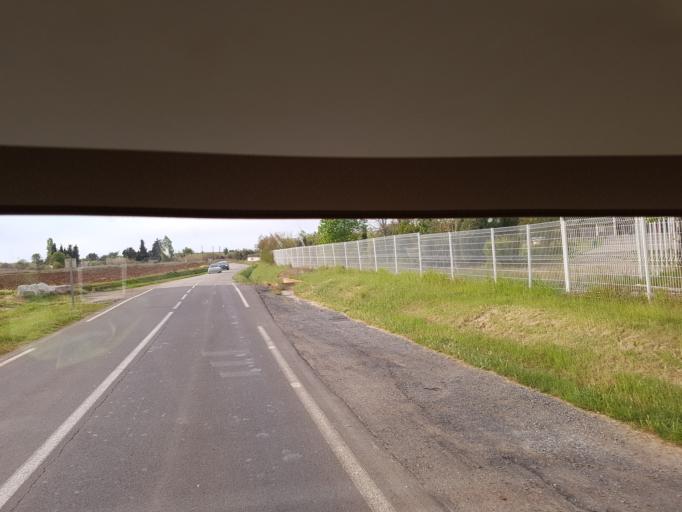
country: FR
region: Languedoc-Roussillon
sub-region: Departement de l'Herault
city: Marseillan
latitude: 43.3629
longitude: 3.5209
